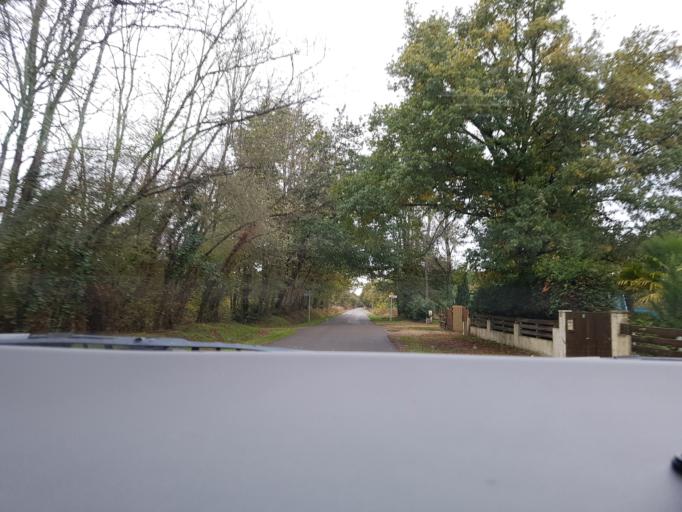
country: FR
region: Aquitaine
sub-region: Departement des Landes
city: Roquefort
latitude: 44.0621
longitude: -0.3523
